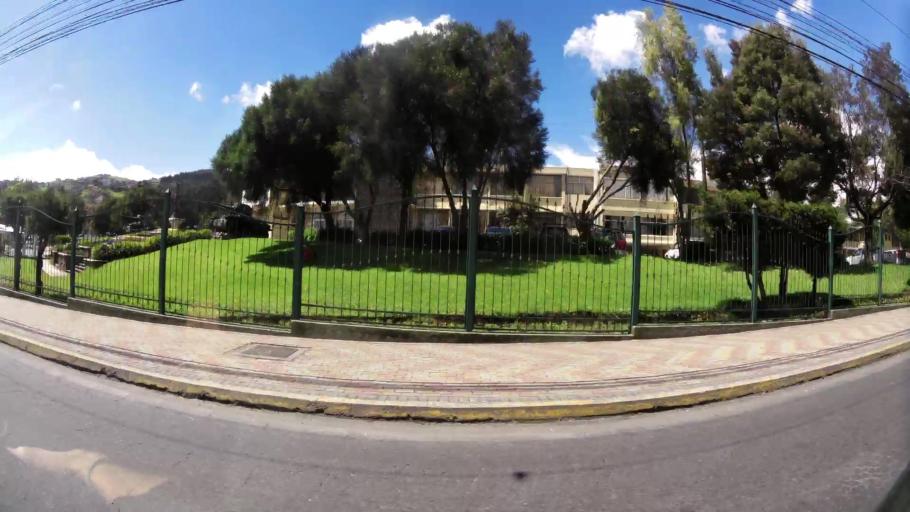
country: EC
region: Pichincha
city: Quito
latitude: -0.2663
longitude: -78.5265
